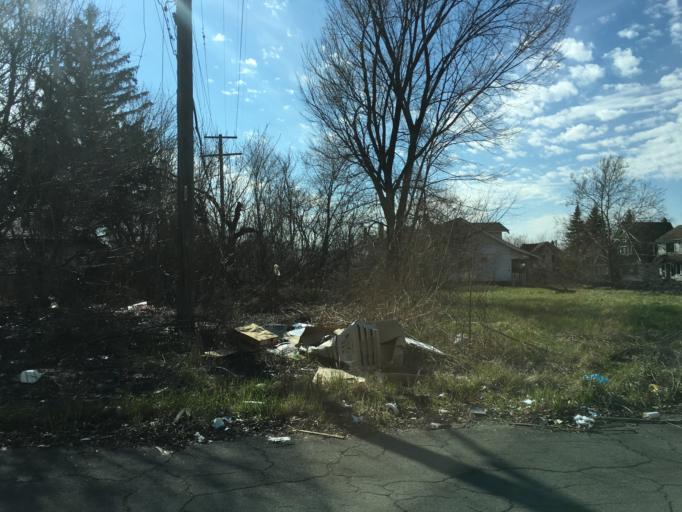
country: US
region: Michigan
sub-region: Macomb County
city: Eastpointe
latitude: 42.4251
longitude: -82.9726
